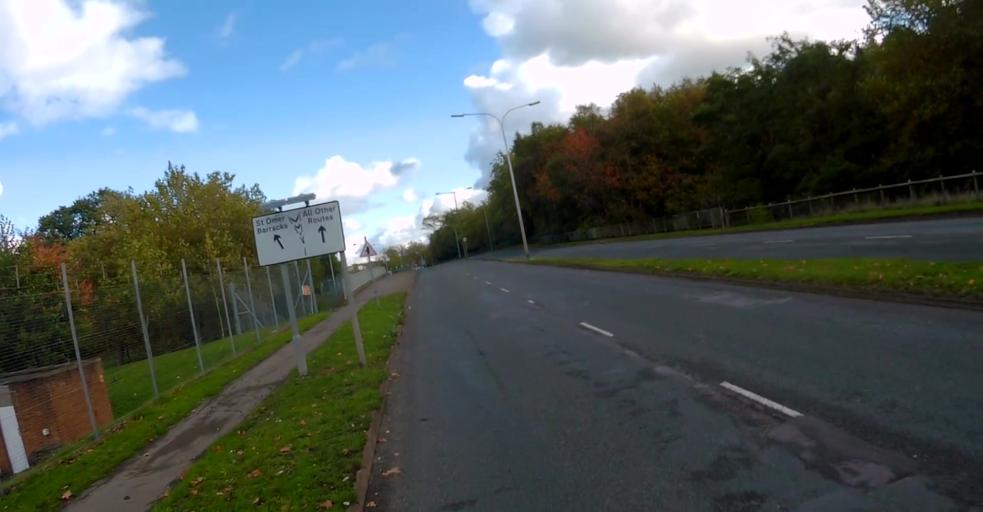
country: GB
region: England
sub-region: Hampshire
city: Aldershot
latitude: 51.2590
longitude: -0.7519
